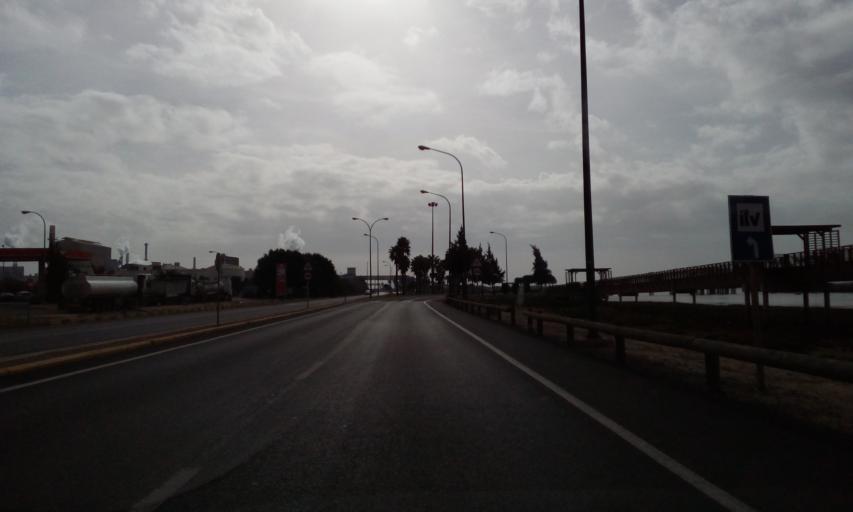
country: ES
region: Andalusia
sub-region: Provincia de Huelva
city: Huelva
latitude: 37.2342
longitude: -6.9534
